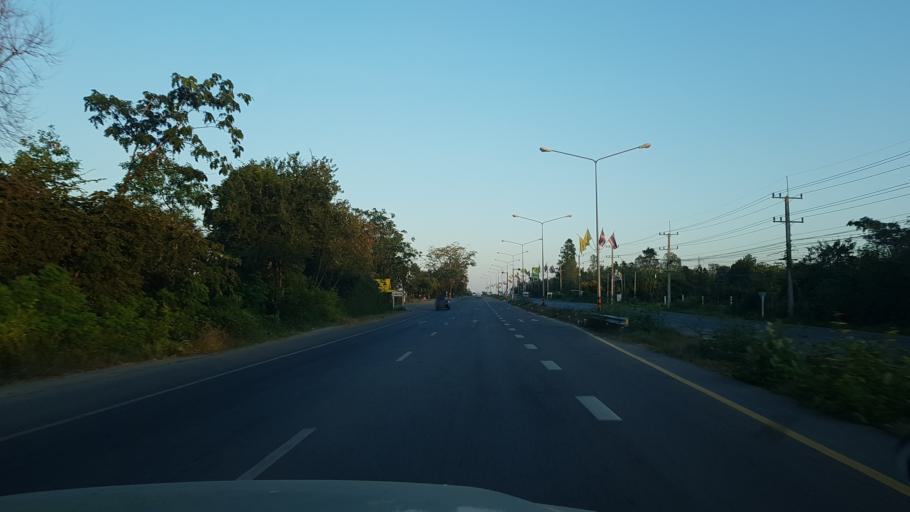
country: TH
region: Khon Kaen
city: Chum Phae
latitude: 16.5777
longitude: 102.0254
